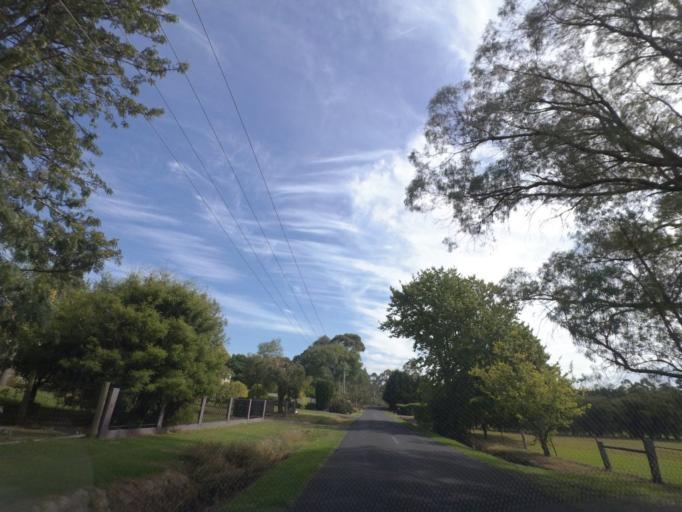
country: AU
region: Victoria
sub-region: Yarra Ranges
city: Healesville
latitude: -37.6433
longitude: 145.5342
